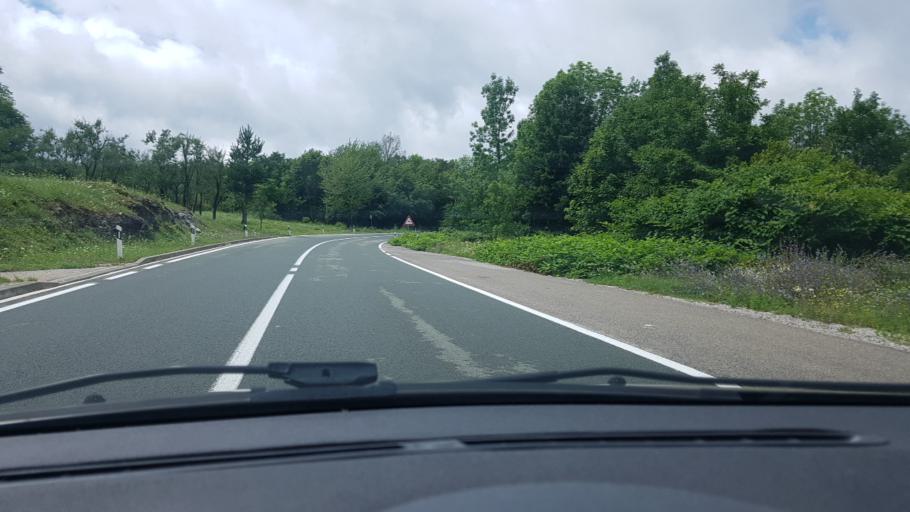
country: HR
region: Licko-Senjska
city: Jezerce
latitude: 44.8849
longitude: 15.6969
